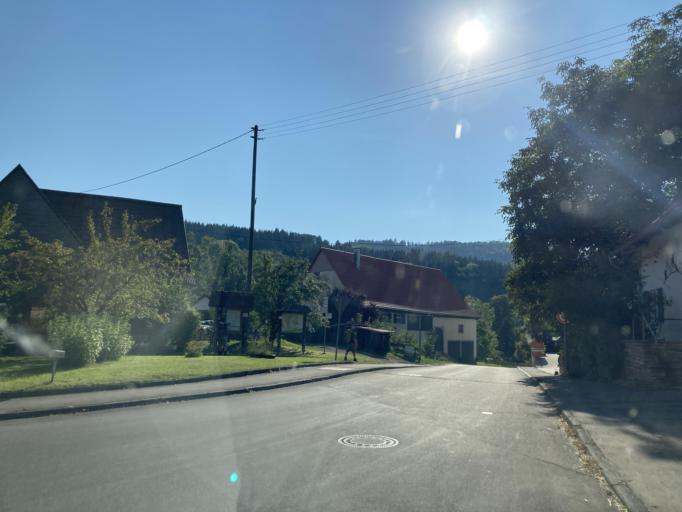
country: DE
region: Baden-Wuerttemberg
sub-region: Freiburg Region
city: Blumberg
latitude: 47.8369
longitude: 8.5014
